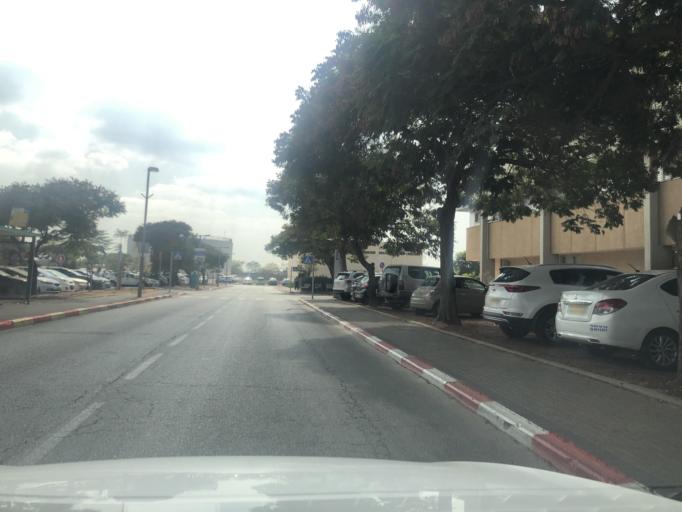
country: IL
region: Tel Aviv
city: Or Yehuda
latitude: 32.0454
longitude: 34.8458
